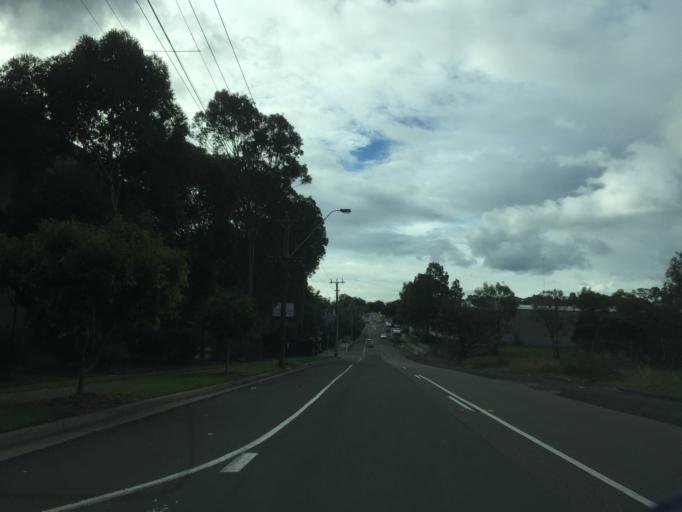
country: AU
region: New South Wales
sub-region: Blacktown
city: Doonside
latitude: -33.7934
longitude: 150.8898
